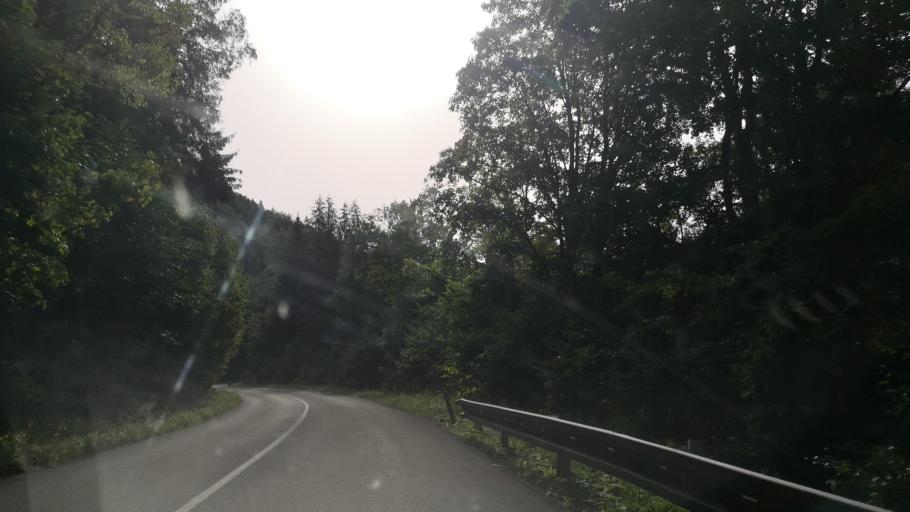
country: SK
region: Banskobystricky
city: Cierny Balog
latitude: 48.6003
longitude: 19.6995
